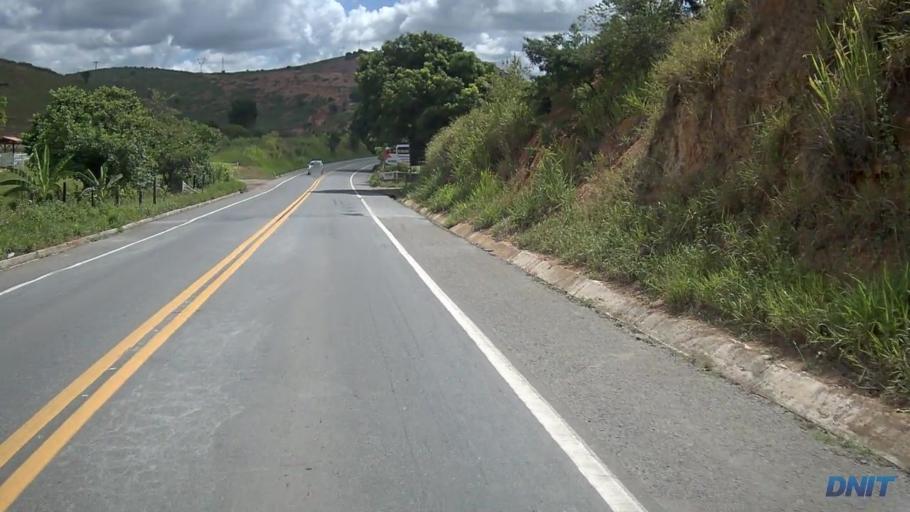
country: BR
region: Minas Gerais
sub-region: Governador Valadares
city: Governador Valadares
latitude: -18.9498
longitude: -42.0703
